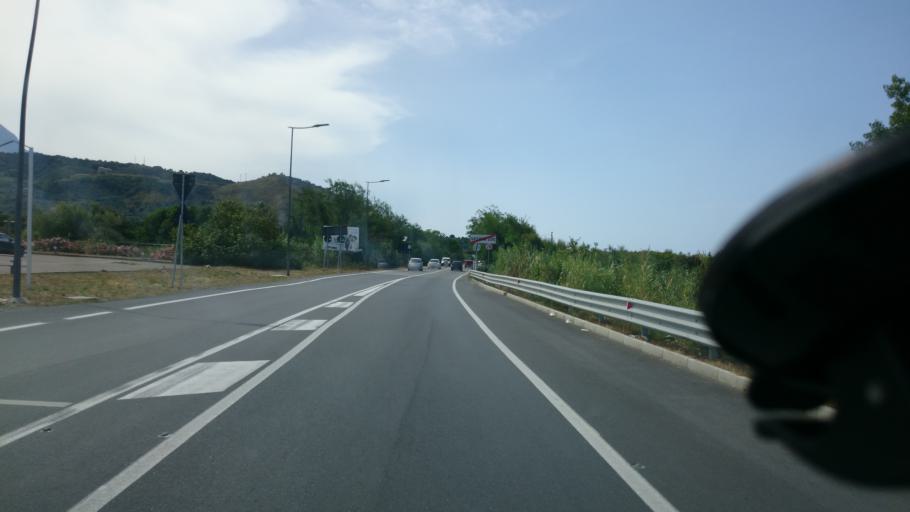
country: IT
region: Calabria
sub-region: Provincia di Cosenza
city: Santa Maria del Cedro
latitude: 39.7304
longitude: 15.8104
